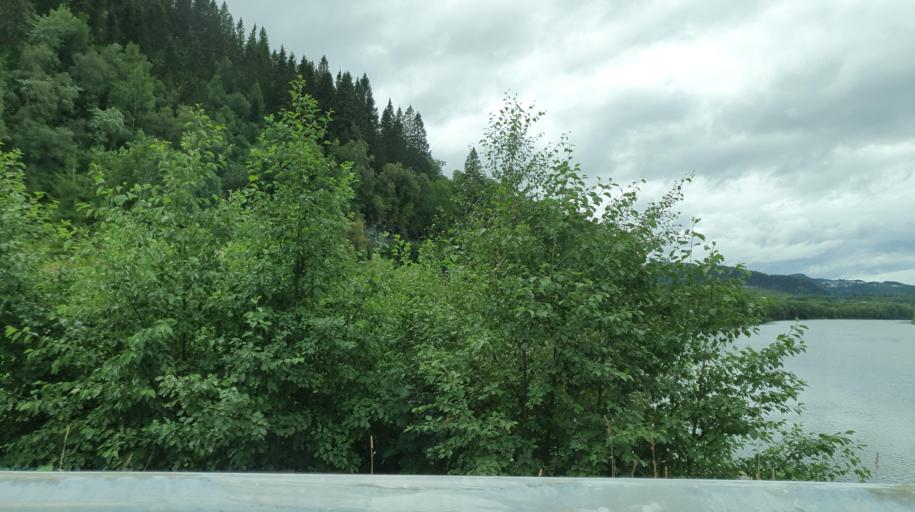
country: NO
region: Nord-Trondelag
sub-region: Stjordal
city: Stjordalshalsen
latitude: 63.4480
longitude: 10.9933
